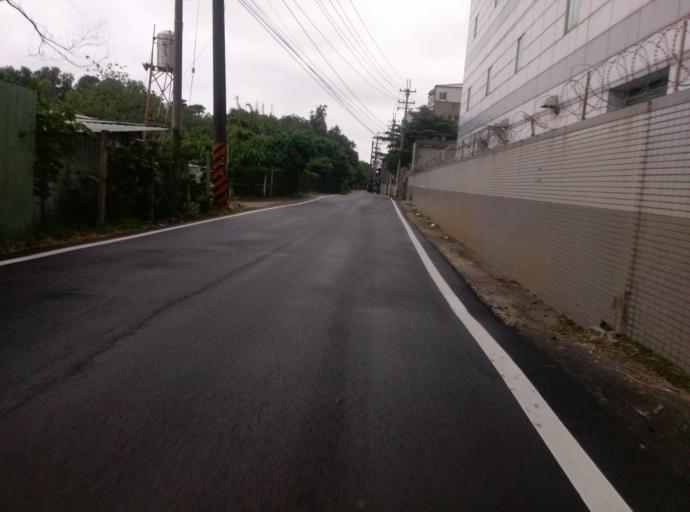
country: TW
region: Taiwan
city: Daxi
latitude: 24.9093
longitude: 121.2408
